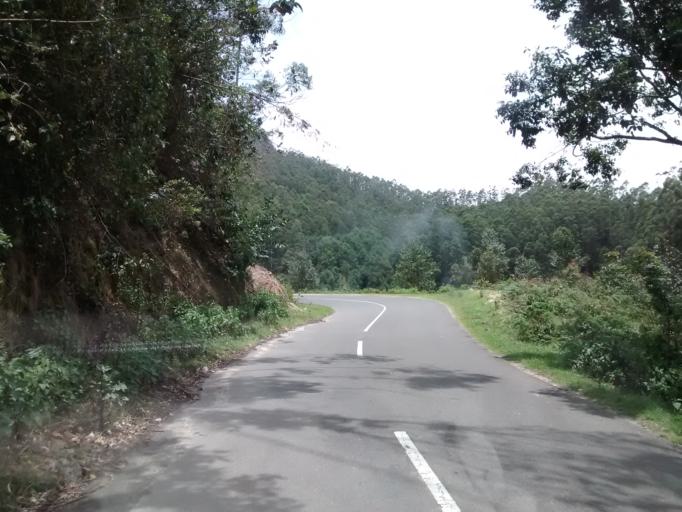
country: IN
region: Kerala
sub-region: Idukki
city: Munnar
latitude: 10.1392
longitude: 77.2044
